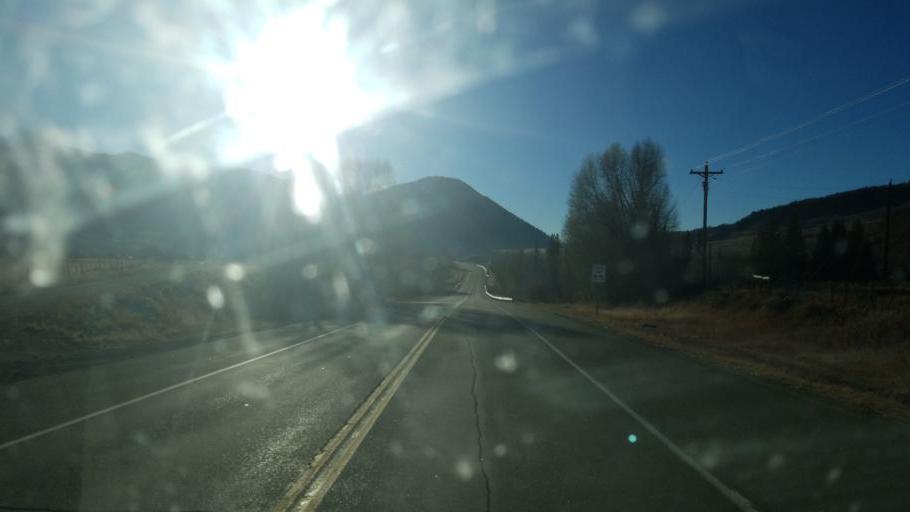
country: US
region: Colorado
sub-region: Gunnison County
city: Crested Butte
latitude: 38.8164
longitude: -106.9071
